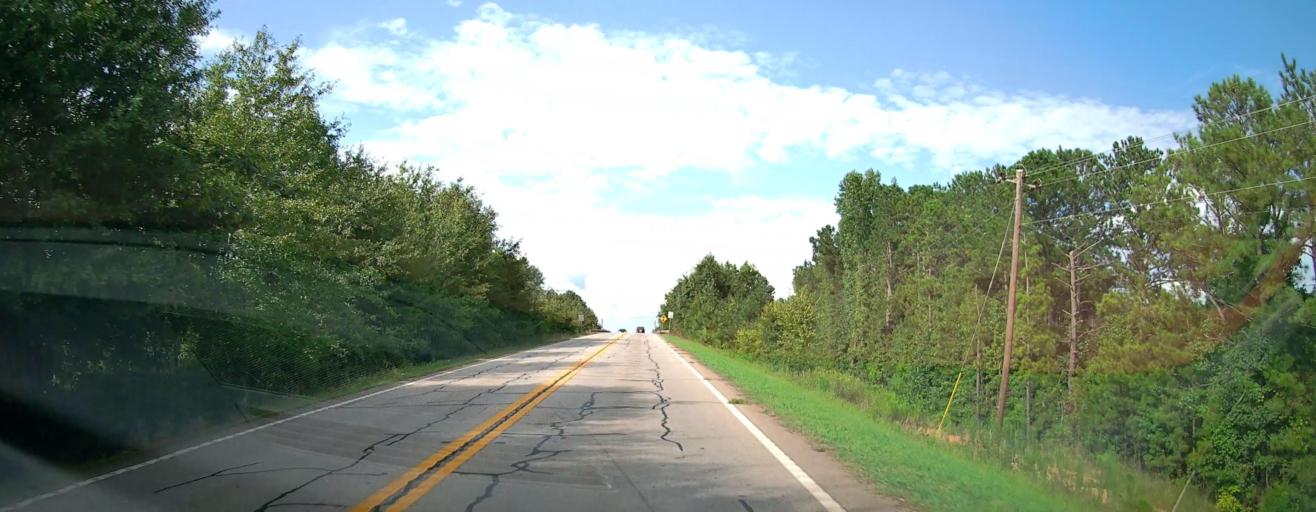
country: US
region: Georgia
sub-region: Meriwether County
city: Manchester
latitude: 32.9804
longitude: -84.5763
